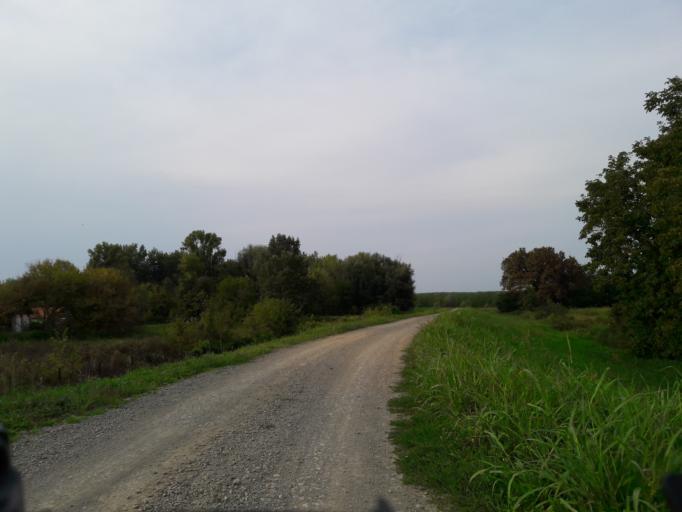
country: HR
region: Osjecko-Baranjska
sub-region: Grad Osijek
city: Osijek
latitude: 45.5702
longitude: 18.6691
